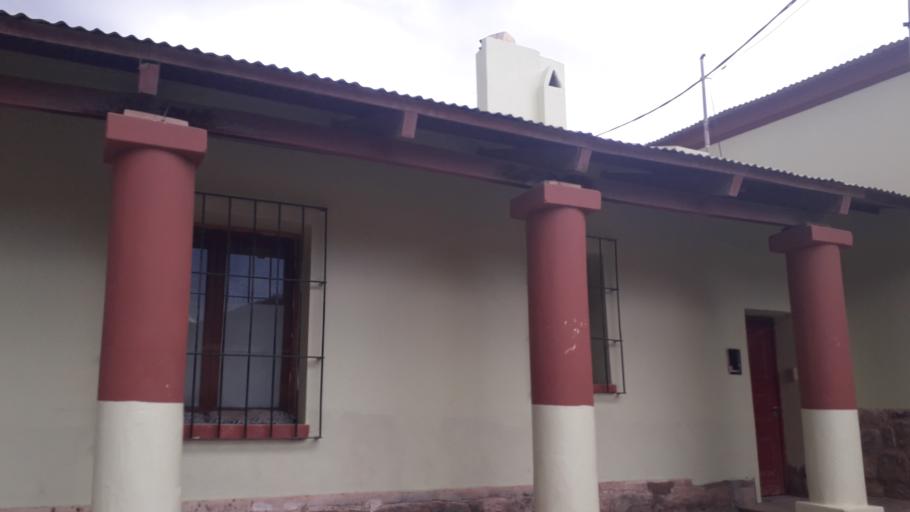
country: AR
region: Jujuy
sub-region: Departamento de Tumbaya
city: Tumbaya
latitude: -23.8580
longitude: -65.4678
